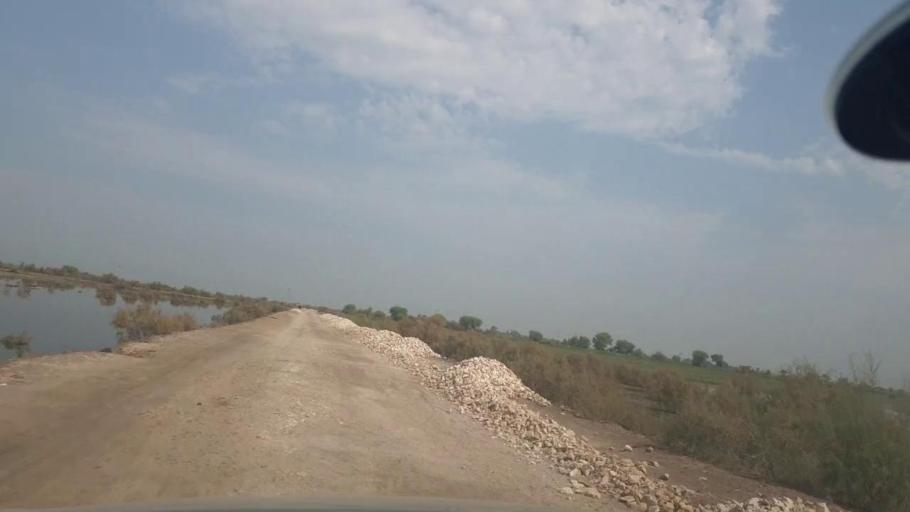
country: PK
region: Balochistan
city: Mehrabpur
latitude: 28.0872
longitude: 68.0977
